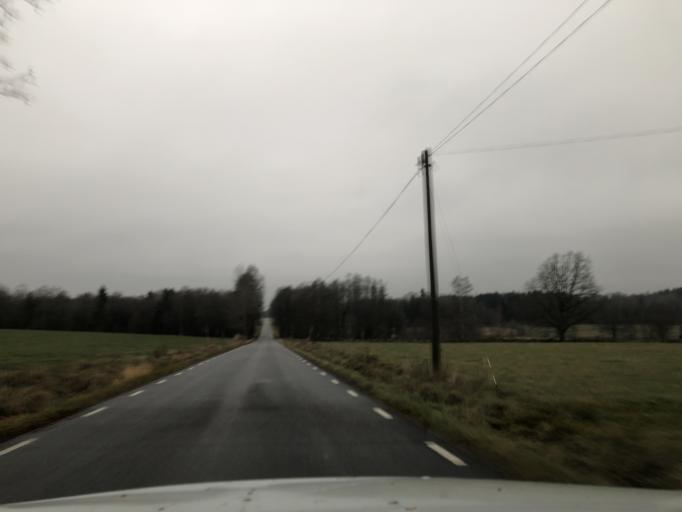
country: SE
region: Vaestra Goetaland
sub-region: Ulricehamns Kommun
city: Ulricehamn
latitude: 57.8362
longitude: 13.3856
